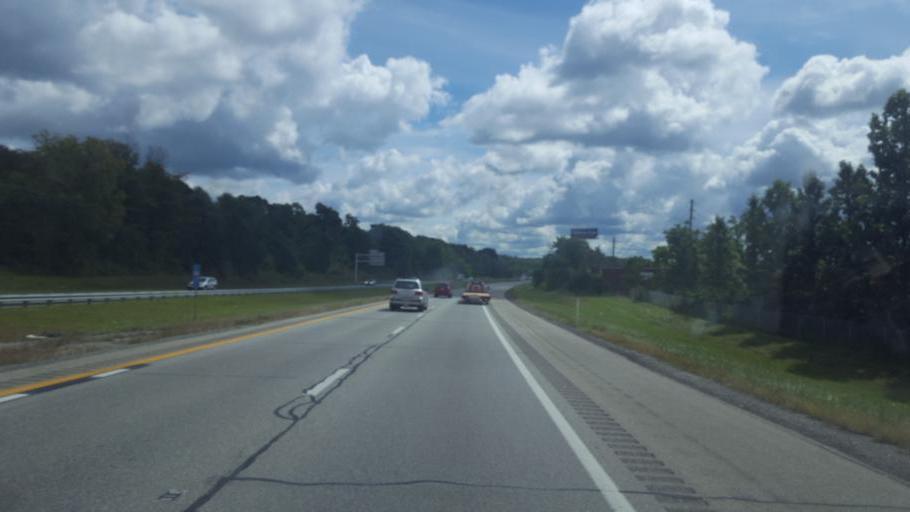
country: US
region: Ohio
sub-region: Cuyahoga County
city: Orange
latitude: 41.4281
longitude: -81.4932
